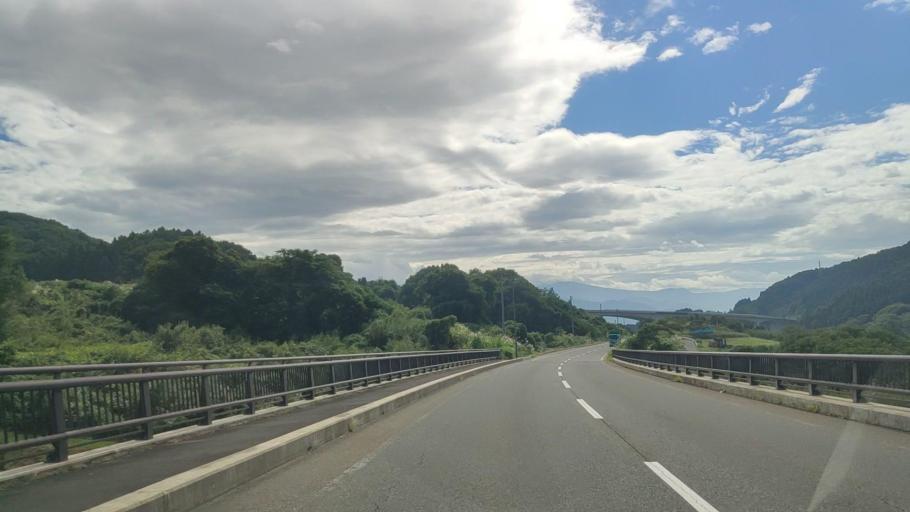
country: JP
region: Nagano
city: Nakano
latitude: 36.7903
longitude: 138.3175
